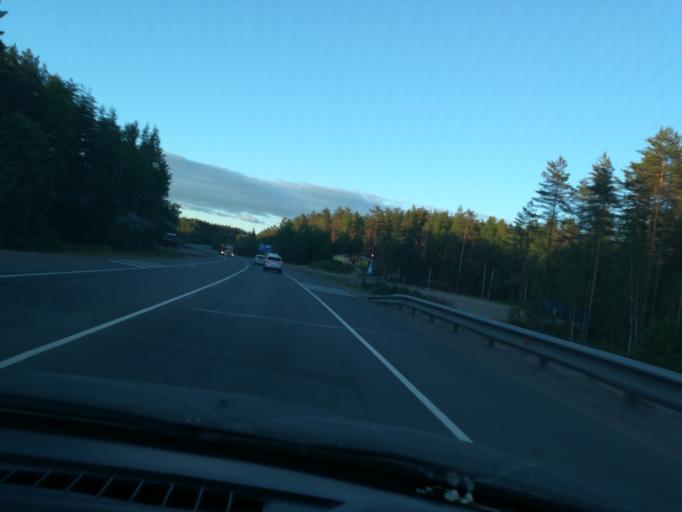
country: RU
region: Leningrad
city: Yakovlevo
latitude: 60.3603
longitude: 29.5438
